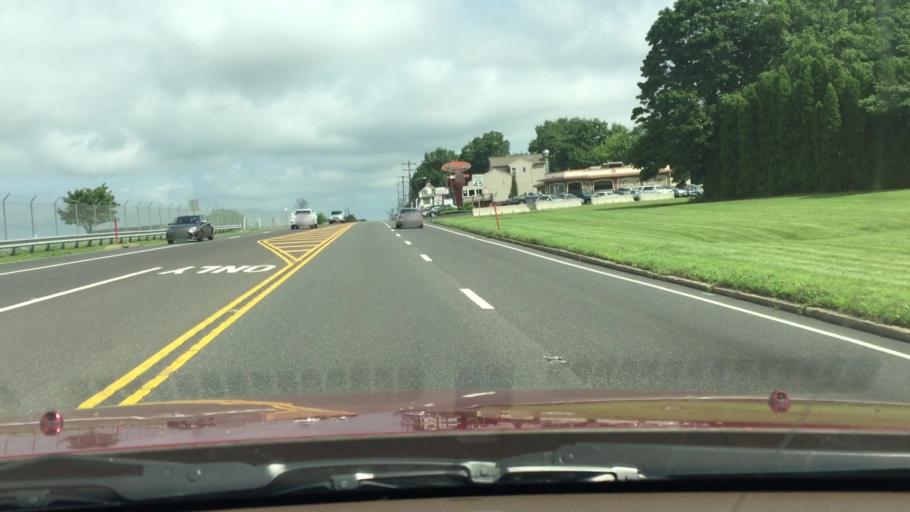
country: US
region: Pennsylvania
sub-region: Montgomery County
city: Horsham
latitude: 40.1914
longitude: -75.1366
